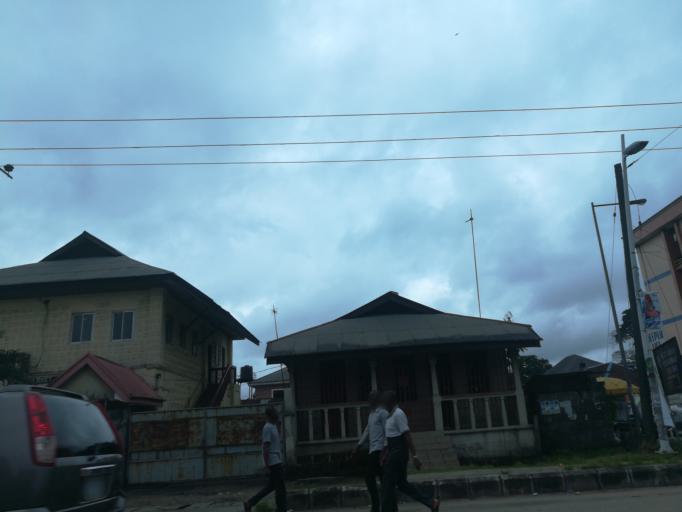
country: NG
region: Rivers
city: Port Harcourt
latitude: 4.7619
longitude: 7.0266
